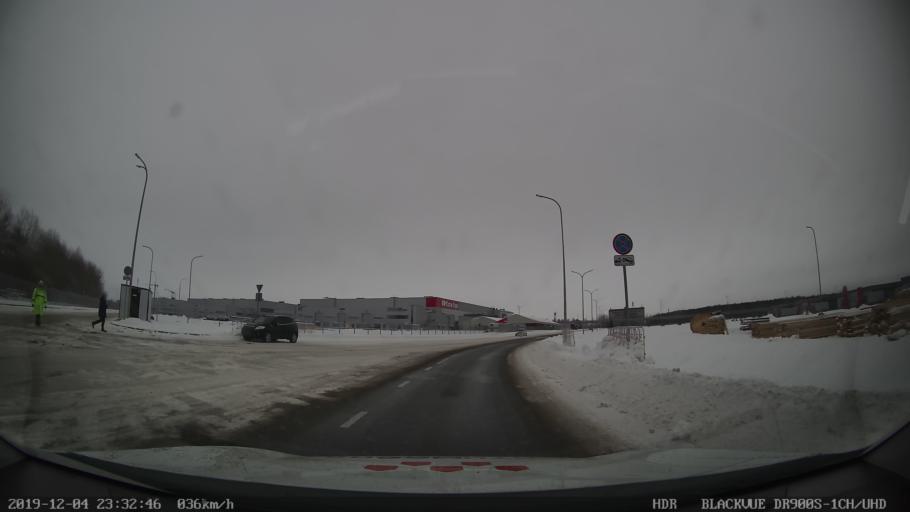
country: RU
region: Tatarstan
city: Stolbishchi
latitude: 55.6153
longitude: 49.2979
